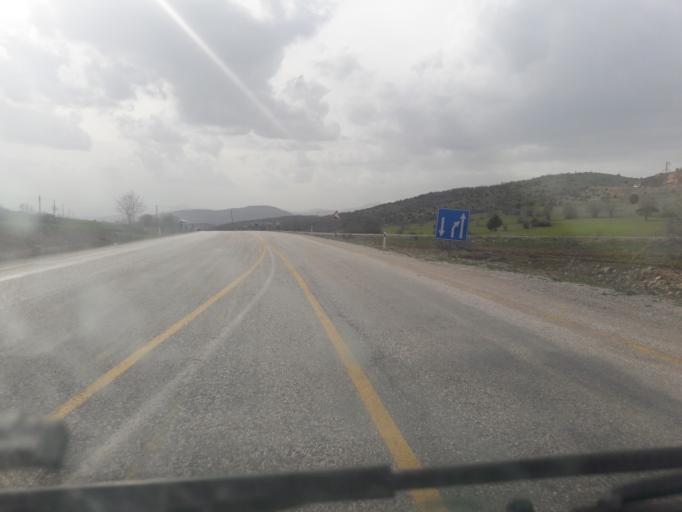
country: TR
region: Gumushane
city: Evren
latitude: 40.1687
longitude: 39.2752
